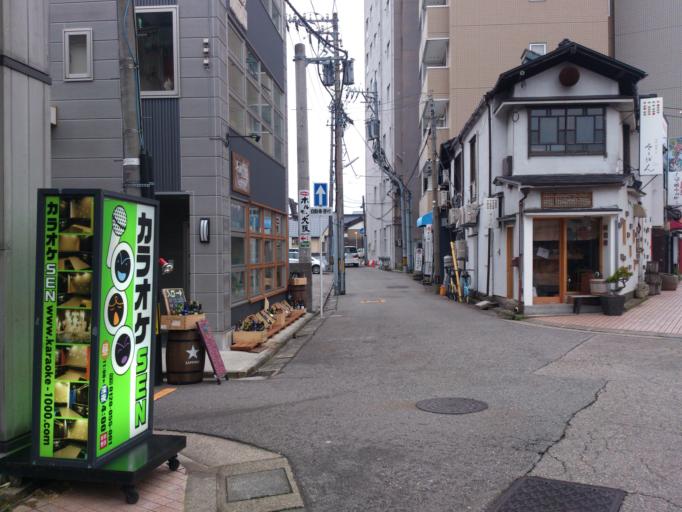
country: JP
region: Ishikawa
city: Kanazawa-shi
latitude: 36.5746
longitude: 136.6479
